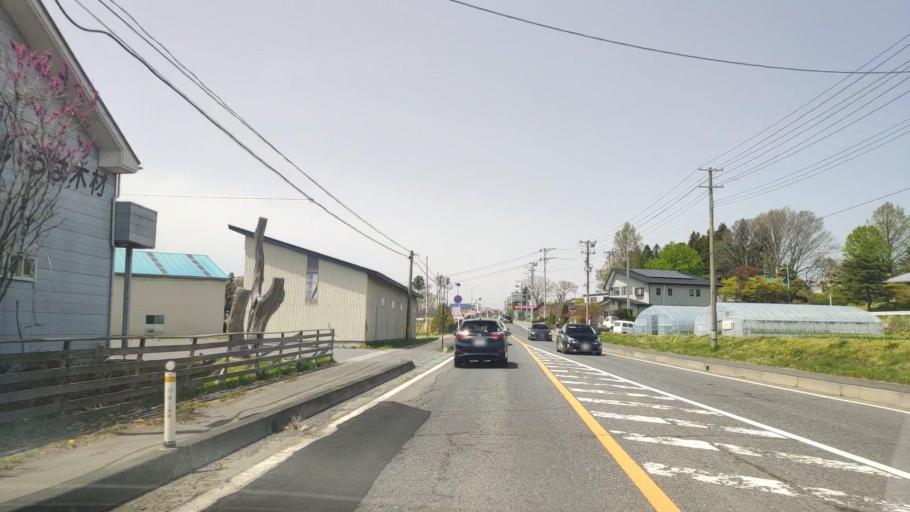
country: JP
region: Aomori
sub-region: Misawa Shi
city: Inuotose
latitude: 40.6056
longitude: 141.2916
